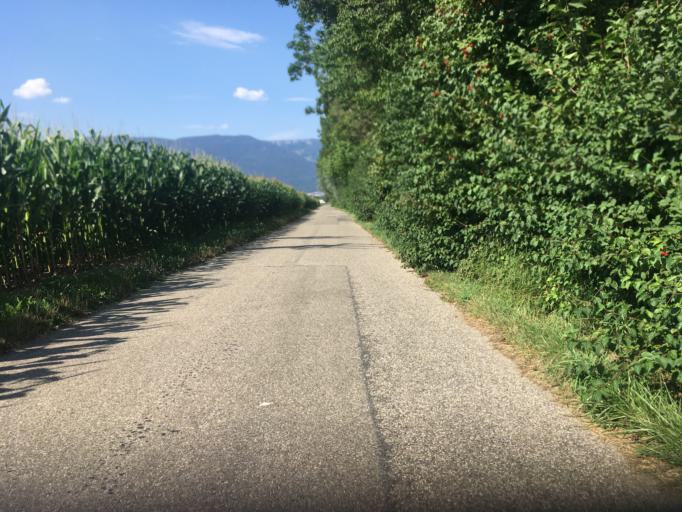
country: CH
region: Bern
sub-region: Biel/Bienne District
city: Lengnau
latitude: 47.1521
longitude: 7.3861
